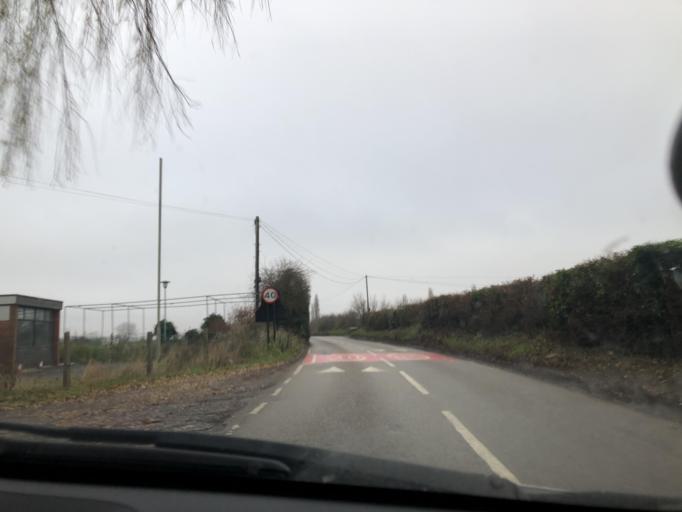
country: GB
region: England
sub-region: Kent
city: Longfield
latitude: 51.4139
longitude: 0.3294
